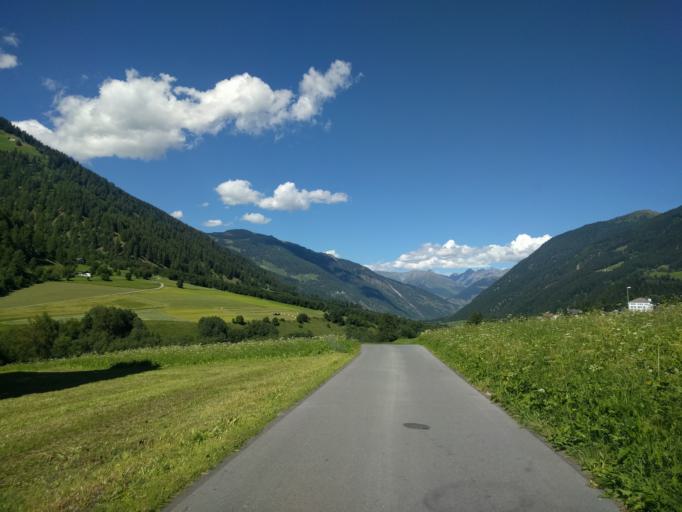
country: IT
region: Trentino-Alto Adige
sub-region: Bolzano
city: Tubre
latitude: 46.6040
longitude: 10.4263
